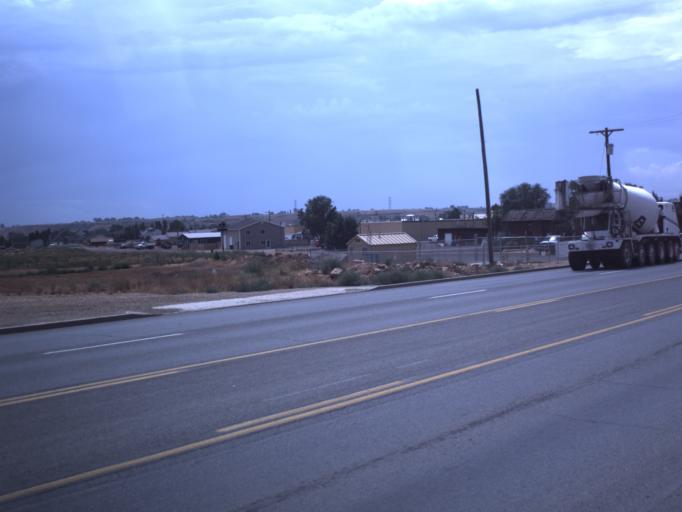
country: US
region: Utah
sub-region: Duchesne County
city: Roosevelt
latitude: 40.2919
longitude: -109.9937
